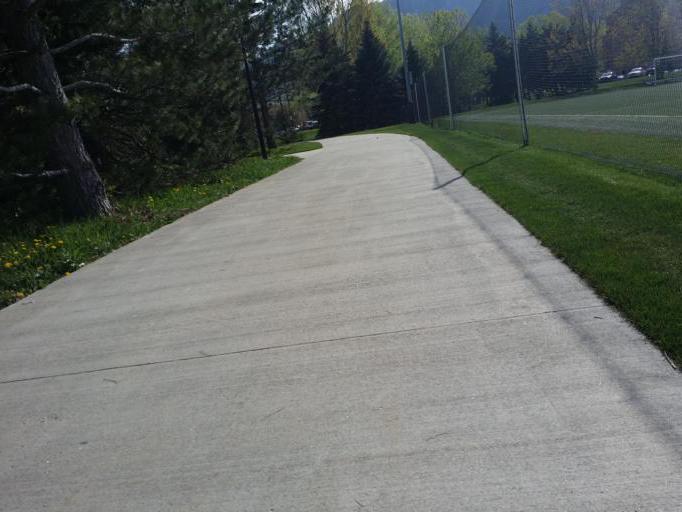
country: US
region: Colorado
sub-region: Boulder County
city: Boulder
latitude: 40.0014
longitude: -105.2601
